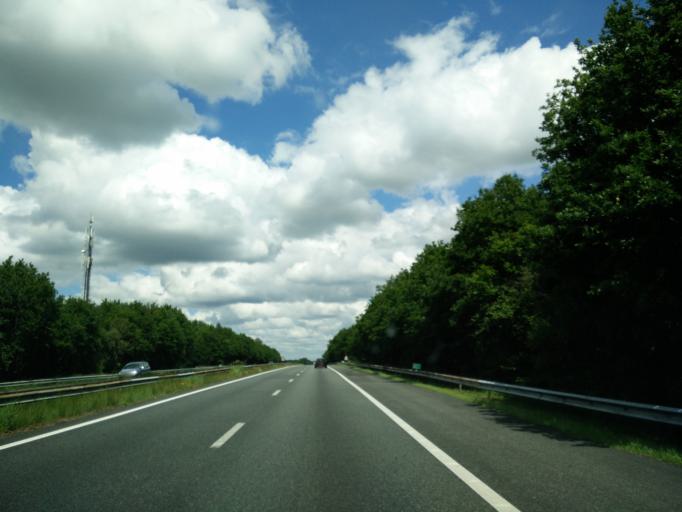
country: NL
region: Drenthe
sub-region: Gemeente Tynaarlo
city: Vries
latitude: 53.0456
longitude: 6.5893
